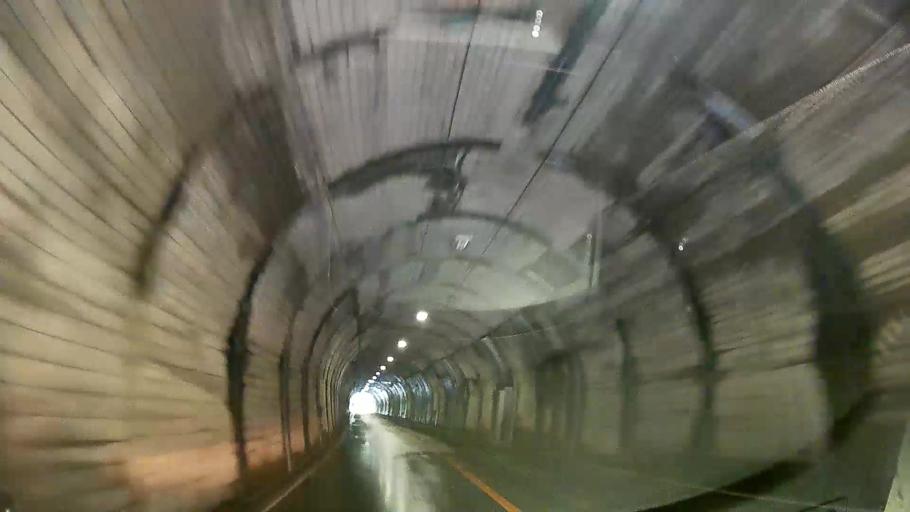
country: JP
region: Oita
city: Hita
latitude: 33.1907
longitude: 130.9944
